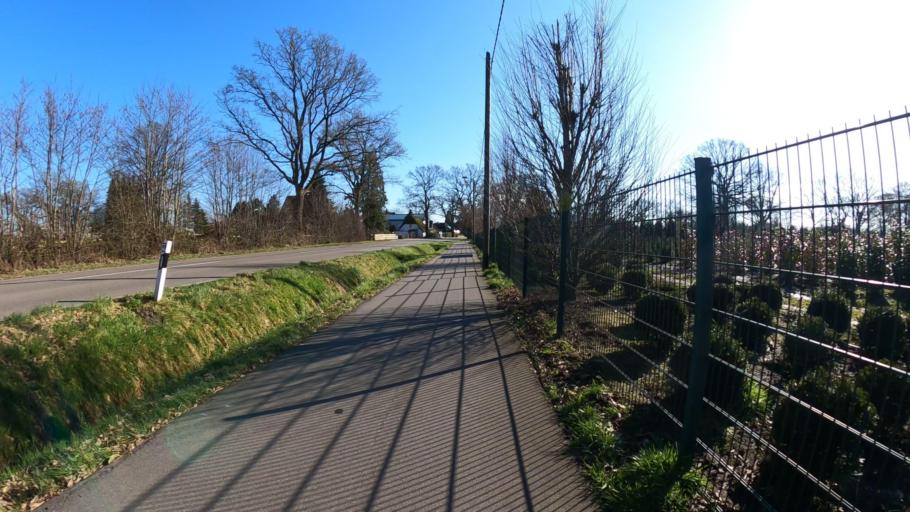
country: DE
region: Schleswig-Holstein
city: Rellingen
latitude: 53.6251
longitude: 9.7974
